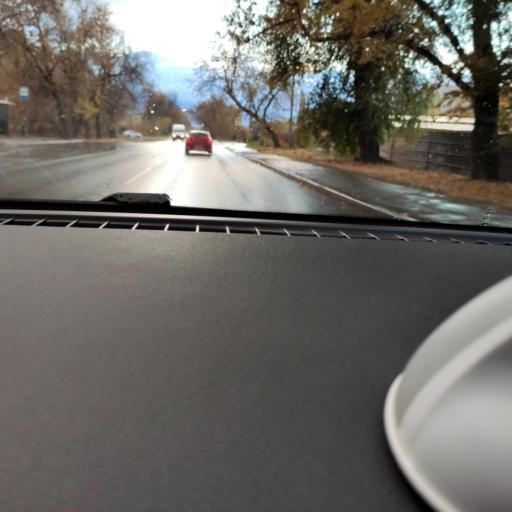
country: RU
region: Samara
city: Smyshlyayevka
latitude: 53.2349
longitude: 50.3142
